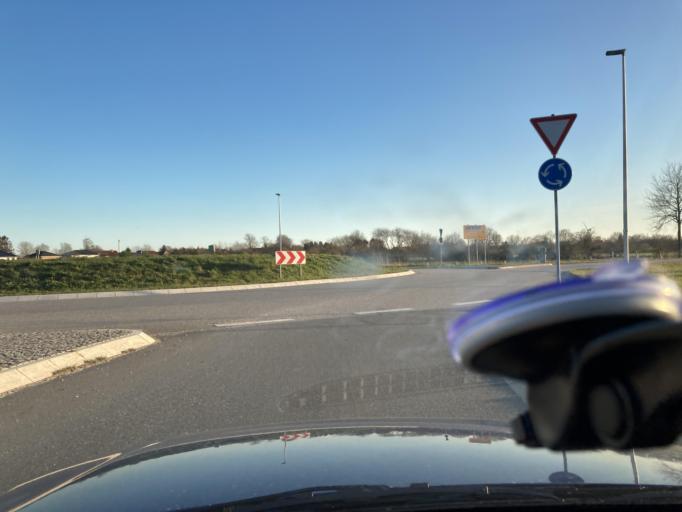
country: DE
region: Schleswig-Holstein
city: Lohe-Rickelshof
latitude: 54.1936
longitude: 9.0730
